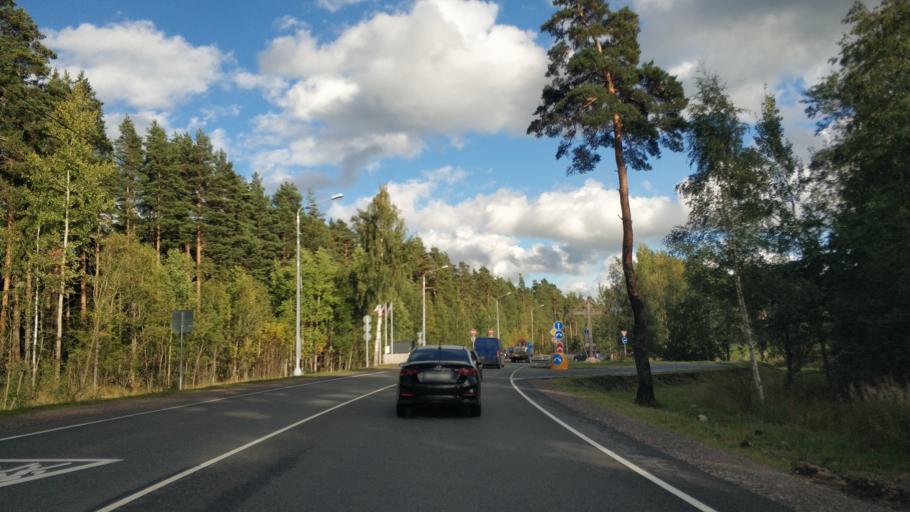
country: RU
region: Leningrad
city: Priozersk
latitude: 61.0091
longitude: 30.1695
